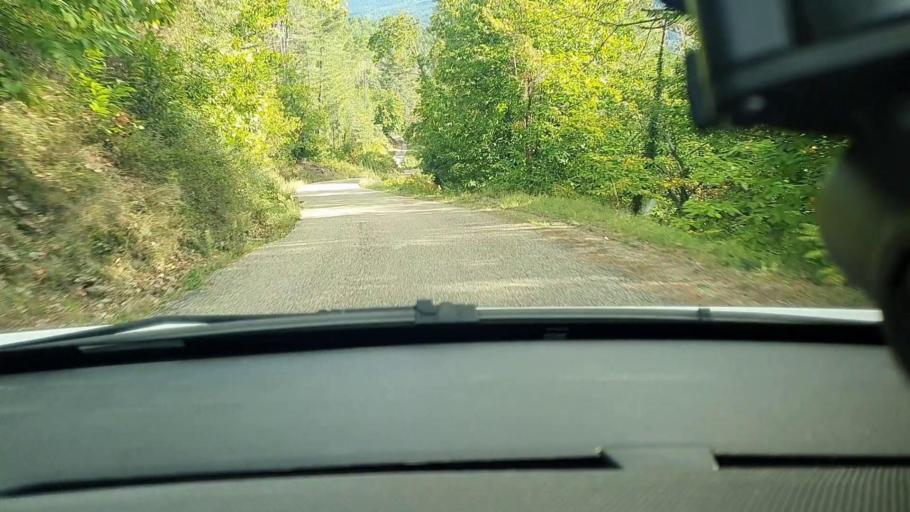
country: FR
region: Languedoc-Roussillon
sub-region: Departement du Gard
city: Besseges
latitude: 44.3524
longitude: 3.9838
